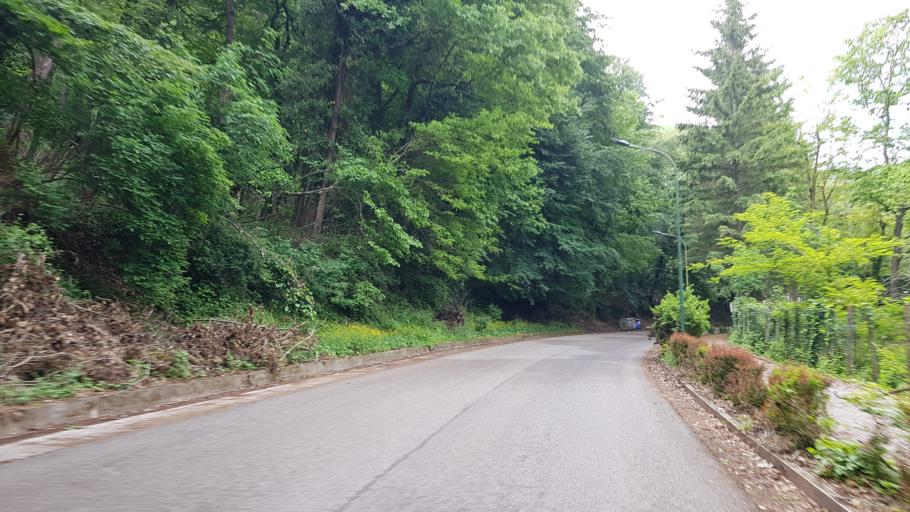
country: IT
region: Basilicate
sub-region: Provincia di Potenza
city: Rionero in Vulture
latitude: 40.9284
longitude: 15.6114
